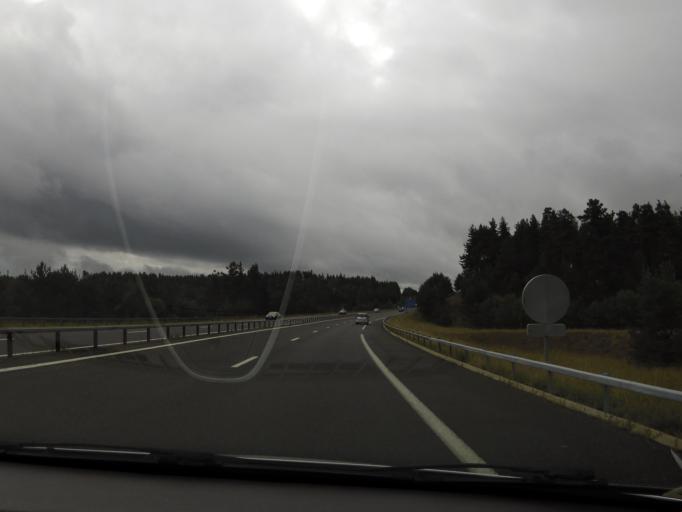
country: FR
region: Languedoc-Roussillon
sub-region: Departement de la Lozere
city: Aumont-Aubrac
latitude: 44.7515
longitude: 3.2894
